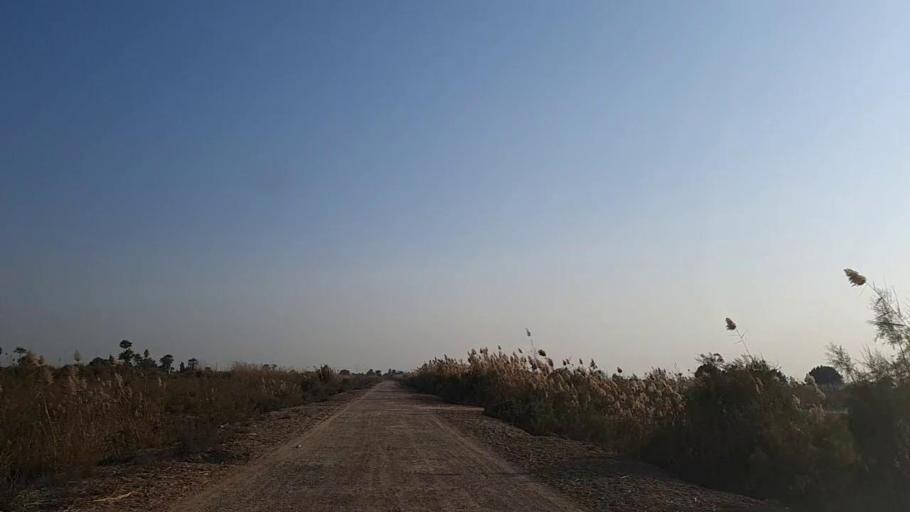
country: PK
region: Sindh
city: Daur
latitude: 26.4220
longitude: 68.3546
